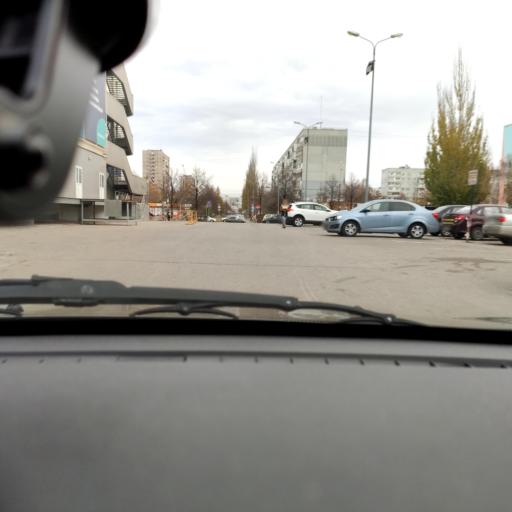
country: RU
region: Samara
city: Tol'yatti
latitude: 53.5333
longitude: 49.3205
